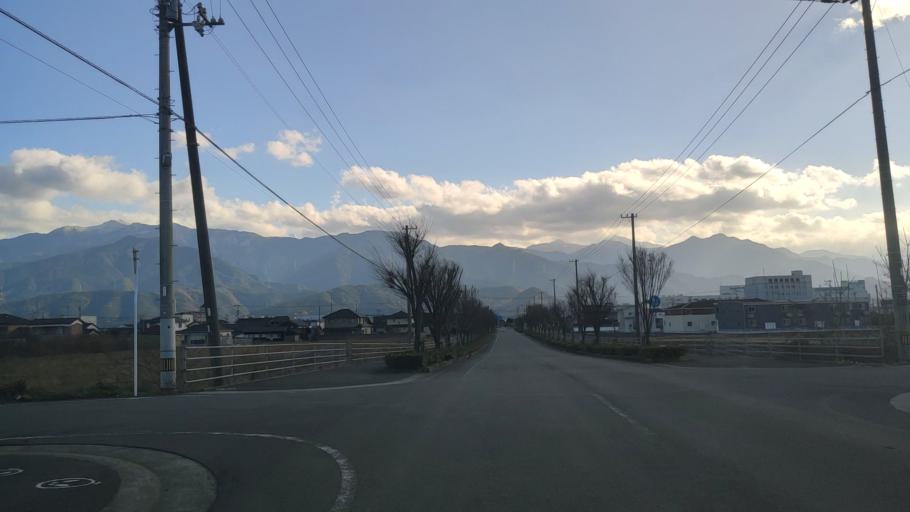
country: JP
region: Ehime
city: Saijo
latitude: 33.9339
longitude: 133.1928
